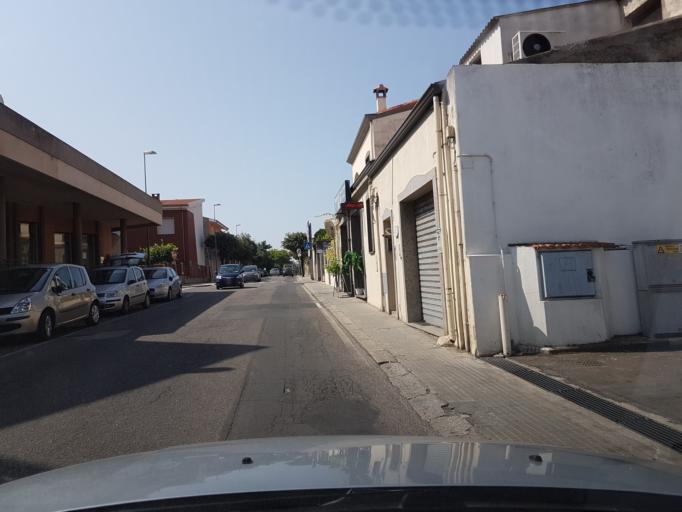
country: IT
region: Sardinia
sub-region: Provincia di Oristano
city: Oristano
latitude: 39.9036
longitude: 8.5955
